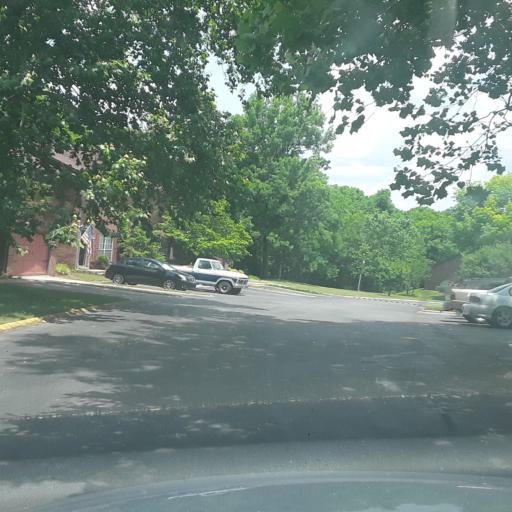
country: US
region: Tennessee
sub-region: Williamson County
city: Brentwood Estates
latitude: 36.0608
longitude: -86.7049
